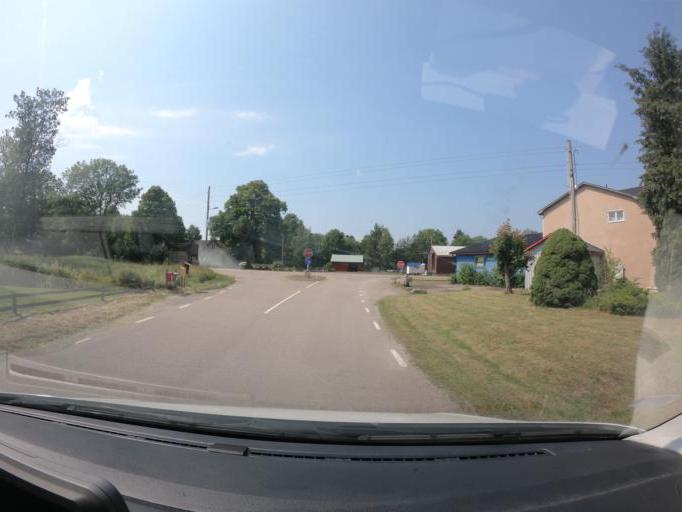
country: SE
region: Kronoberg
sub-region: Markaryds Kommun
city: Markaryd
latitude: 56.3993
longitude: 13.5238
